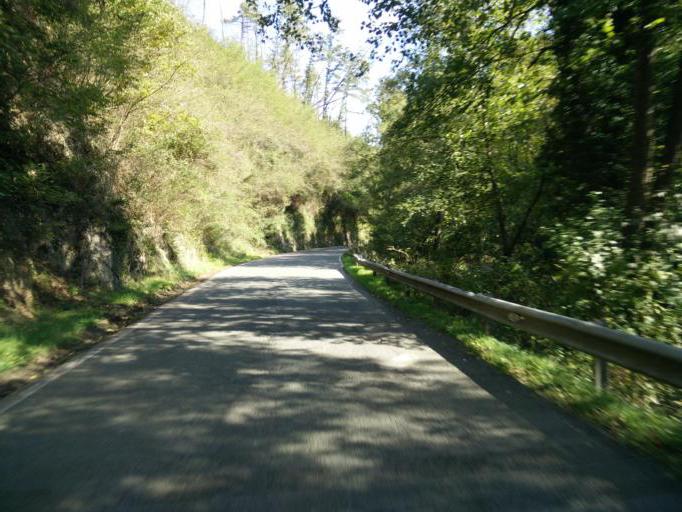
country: IT
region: Liguria
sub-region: Provincia di La Spezia
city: Carrodano
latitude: 44.2417
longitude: 9.6722
